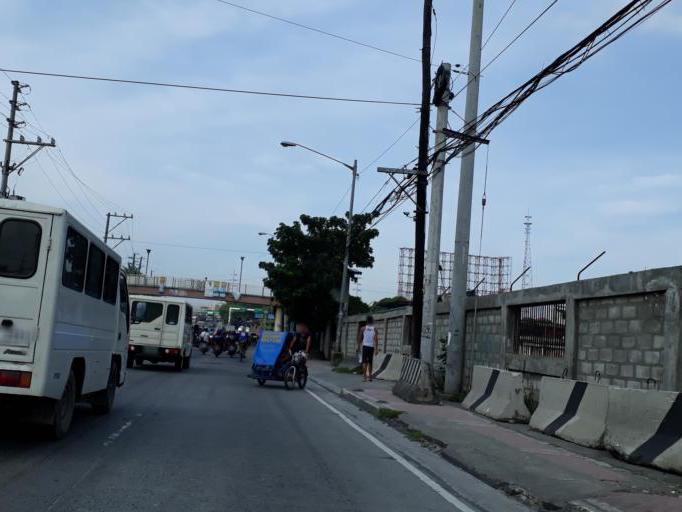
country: PH
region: Calabarzon
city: Del Monte
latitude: 14.6642
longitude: 121.0029
